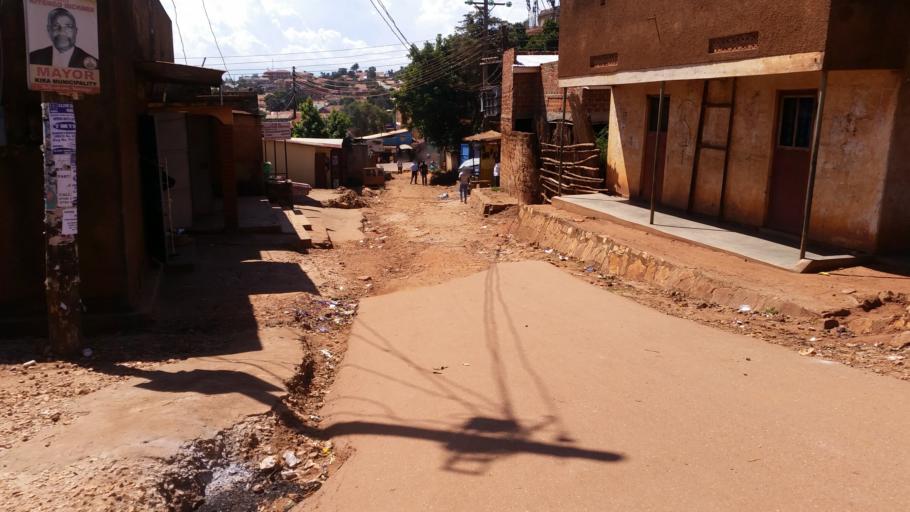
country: UG
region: Central Region
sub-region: Wakiso District
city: Kireka
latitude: 0.3441
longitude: 32.6472
